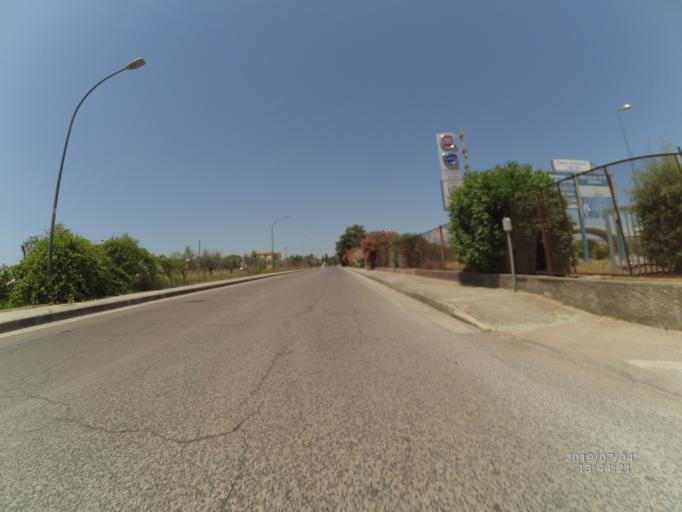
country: IT
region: Latium
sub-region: Provincia di Latina
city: San Felice Circeo
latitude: 41.2544
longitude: 13.0932
